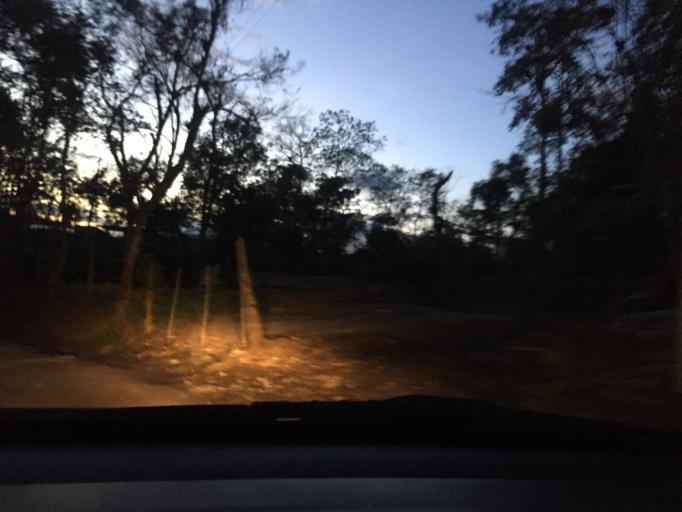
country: CO
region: Cundinamarca
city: Zipacon
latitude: 4.7260
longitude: -74.4187
